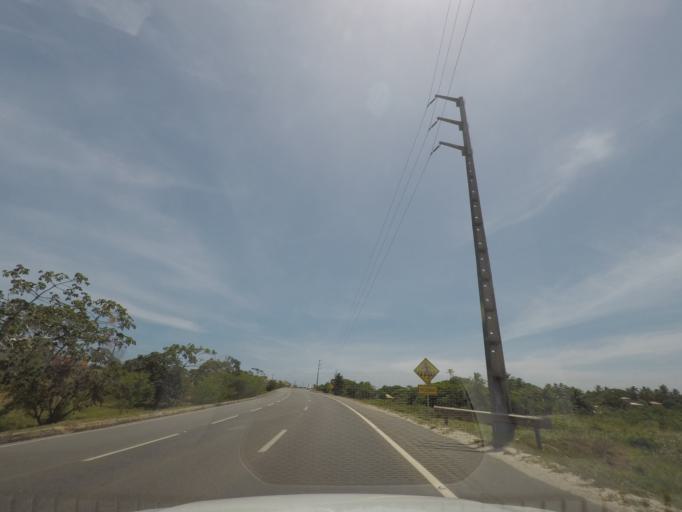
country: BR
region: Bahia
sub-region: Camacari
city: Camacari
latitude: -12.6557
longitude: -38.0874
